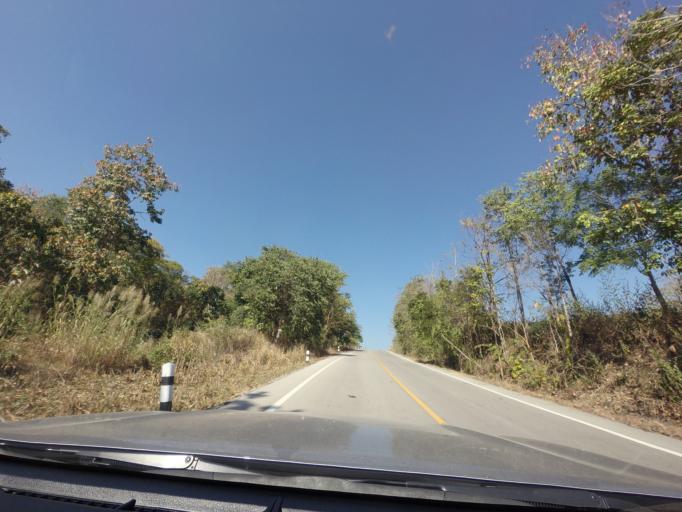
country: TH
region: Lampang
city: Chae Hom
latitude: 18.5704
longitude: 99.6253
